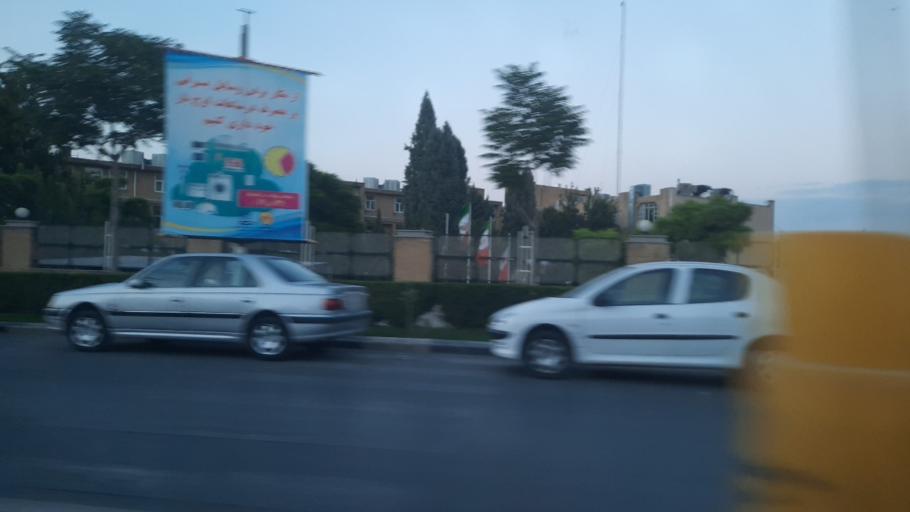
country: IR
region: Markazi
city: Arak
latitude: 34.0750
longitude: 49.7030
